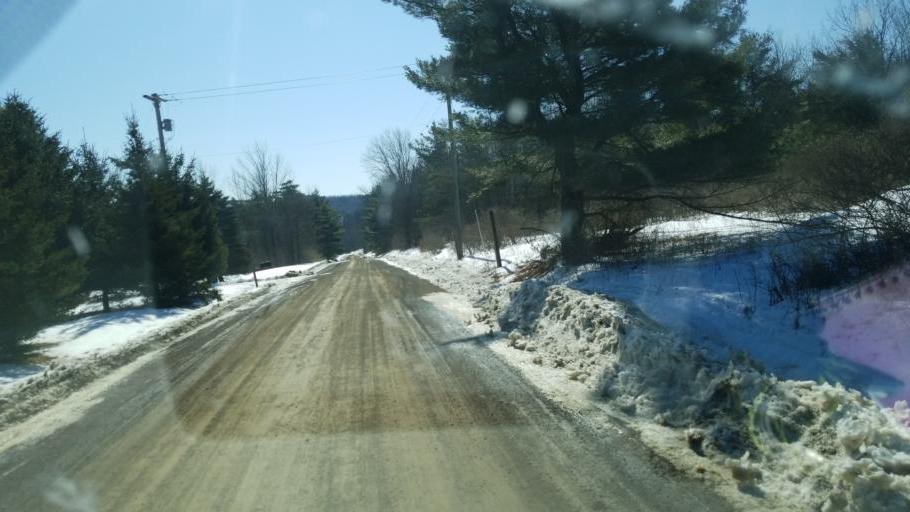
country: US
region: New York
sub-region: Allegany County
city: Alfred
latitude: 42.2507
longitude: -77.7318
